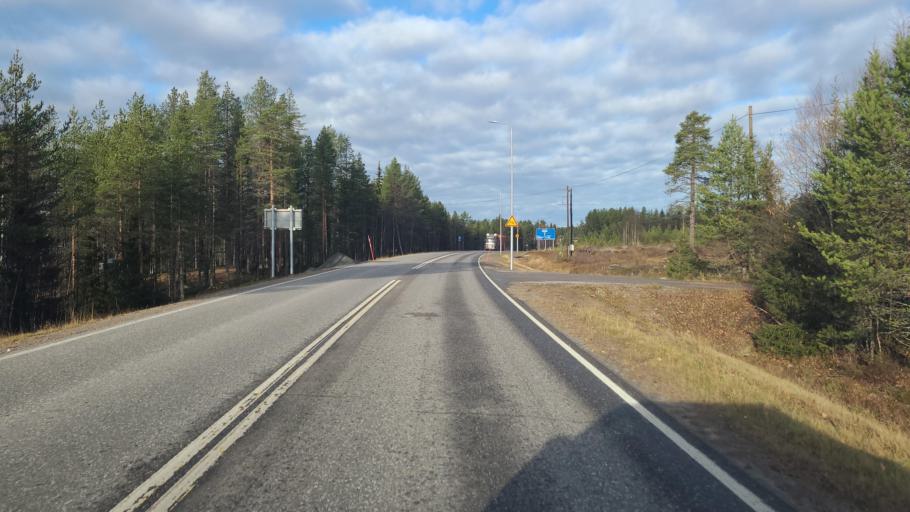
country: FI
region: Lapland
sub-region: Itae-Lappi
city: Posio
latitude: 66.1051
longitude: 28.1833
